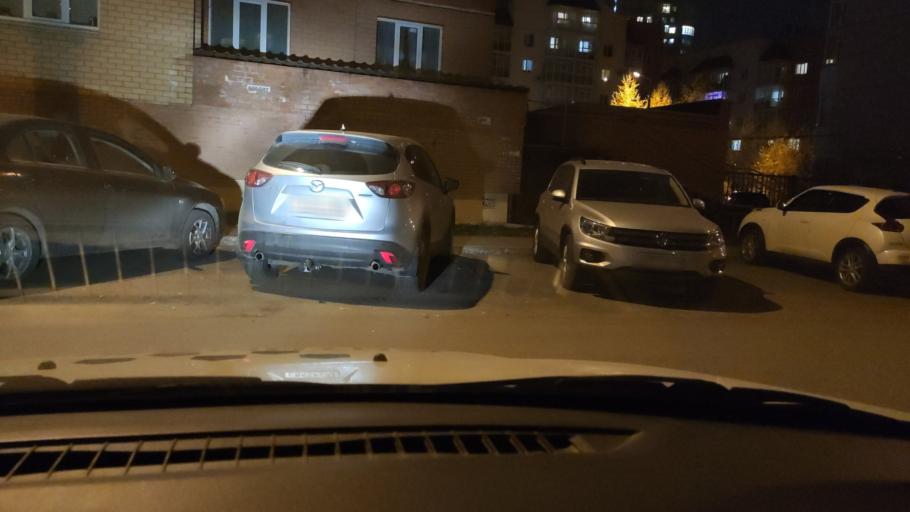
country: RU
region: Perm
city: Perm
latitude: 57.9961
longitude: 56.2286
